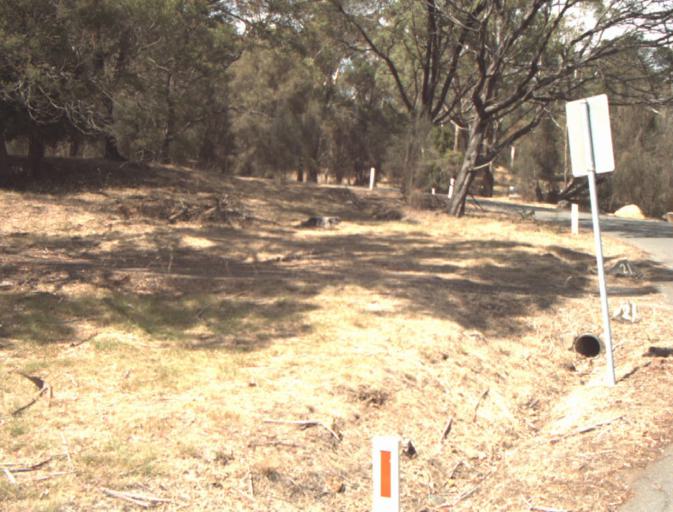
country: AU
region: Tasmania
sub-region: Launceston
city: West Launceston
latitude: -41.4493
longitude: 147.1202
